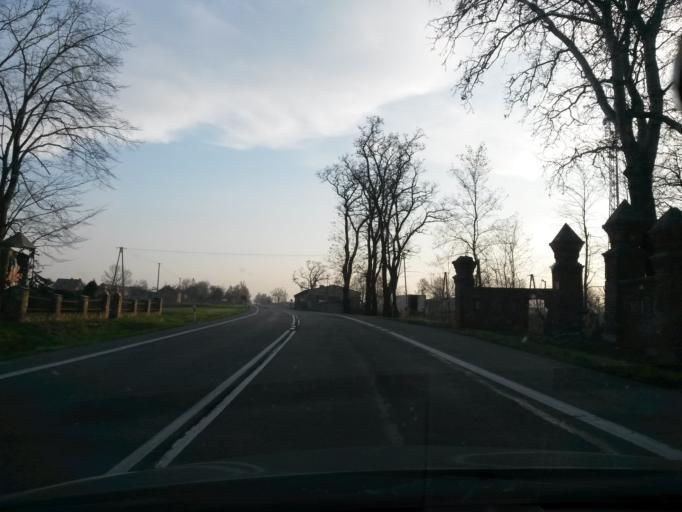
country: PL
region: Lodz Voivodeship
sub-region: Powiat wieruszowski
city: Walichnowy
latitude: 51.3008
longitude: 18.3798
